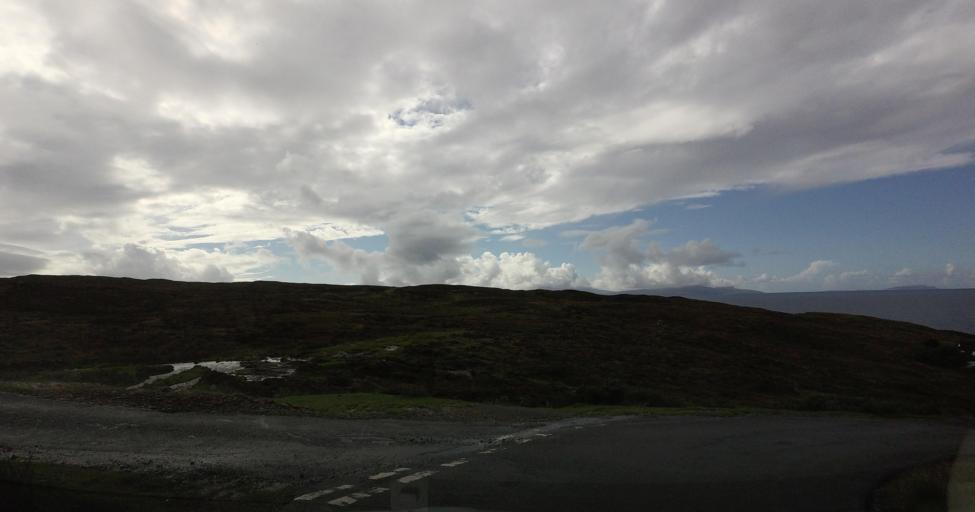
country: GB
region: Scotland
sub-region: Highland
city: Isle of Skye
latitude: 57.1457
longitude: -6.1031
